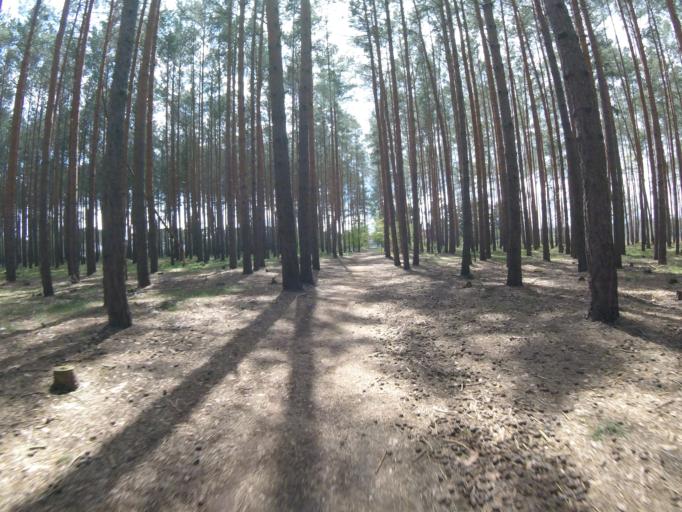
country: DE
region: Brandenburg
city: Bestensee
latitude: 52.2316
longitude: 13.6390
